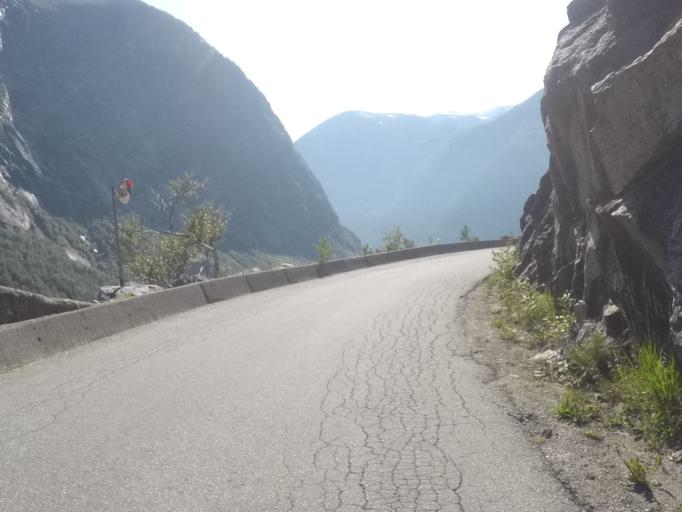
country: NO
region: Hordaland
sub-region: Odda
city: Odda
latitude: 60.1201
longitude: 6.5874
